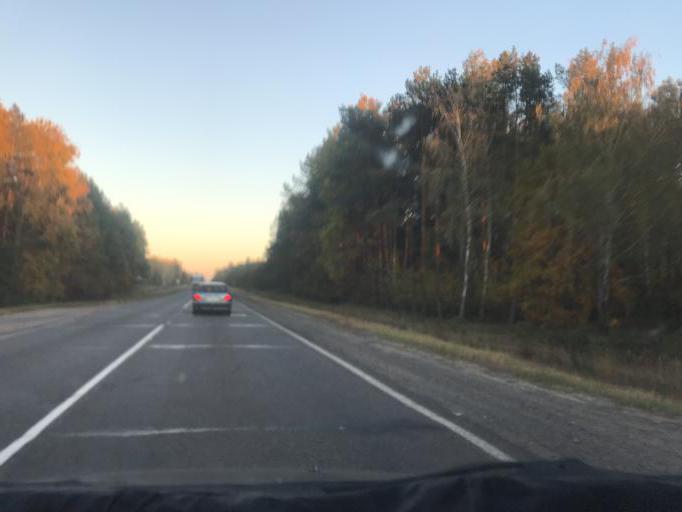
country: BY
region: Gomel
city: Mazyr
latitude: 52.2000
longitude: 29.0883
